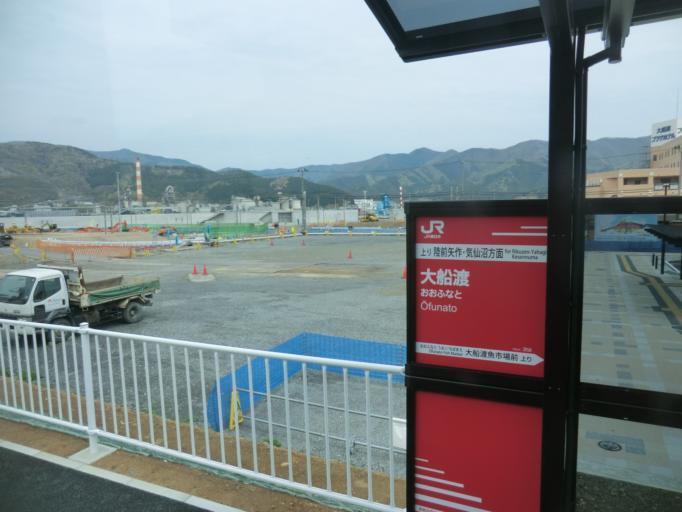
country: JP
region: Iwate
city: Ofunato
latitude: 39.0629
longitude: 141.7209
